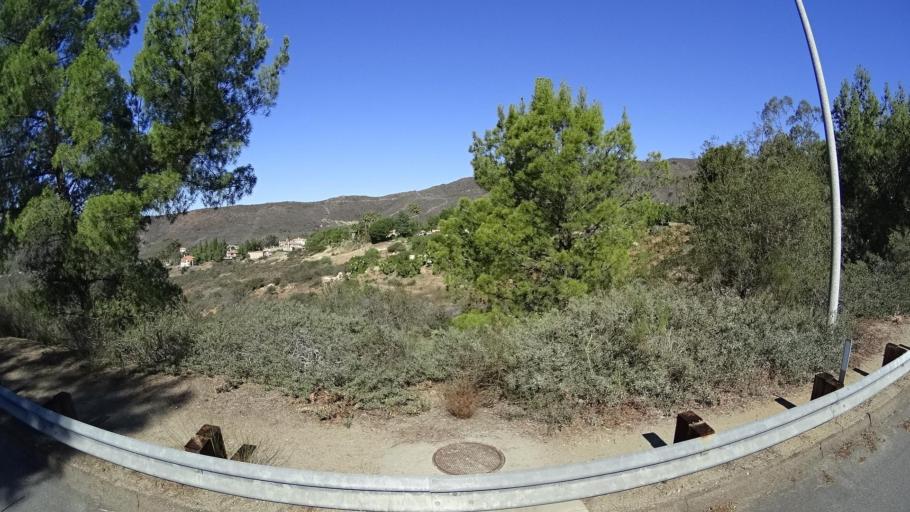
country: US
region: California
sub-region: San Diego County
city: Jamul
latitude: 32.7364
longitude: -116.8546
